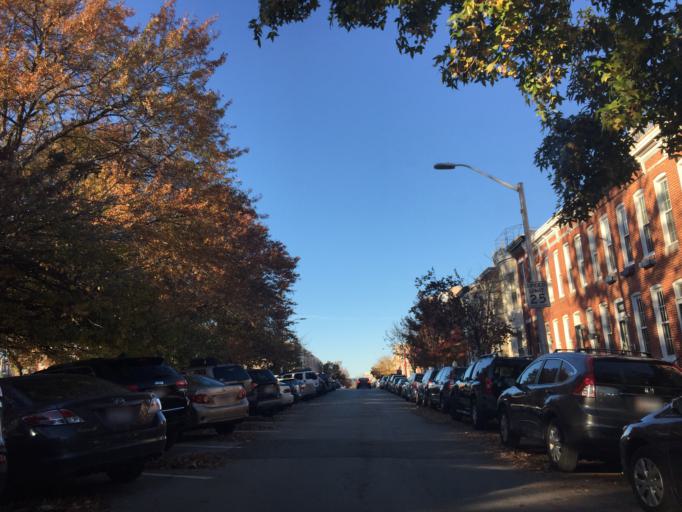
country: US
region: Maryland
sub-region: City of Baltimore
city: Baltimore
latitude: 39.2710
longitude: -76.6065
